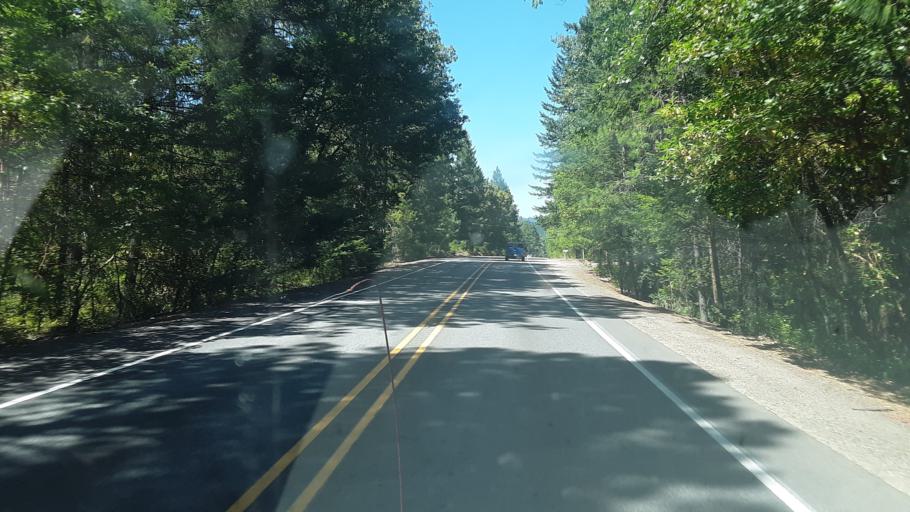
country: US
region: Oregon
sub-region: Josephine County
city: Cave Junction
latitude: 42.3029
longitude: -123.6112
